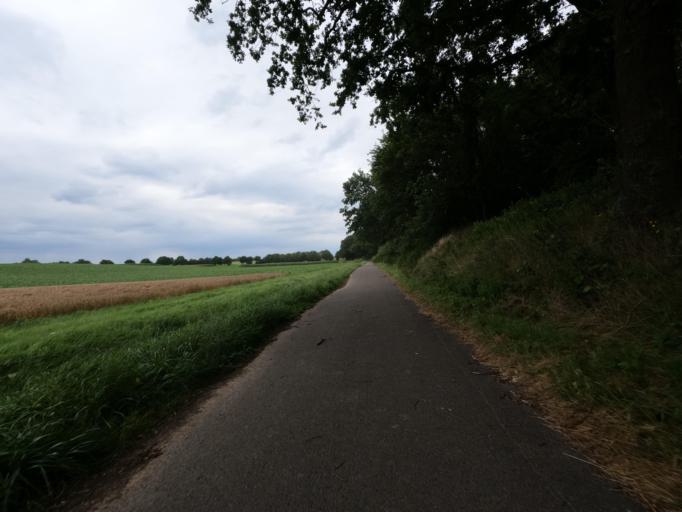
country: DE
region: North Rhine-Westphalia
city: Geilenkirchen
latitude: 50.9784
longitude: 6.1761
